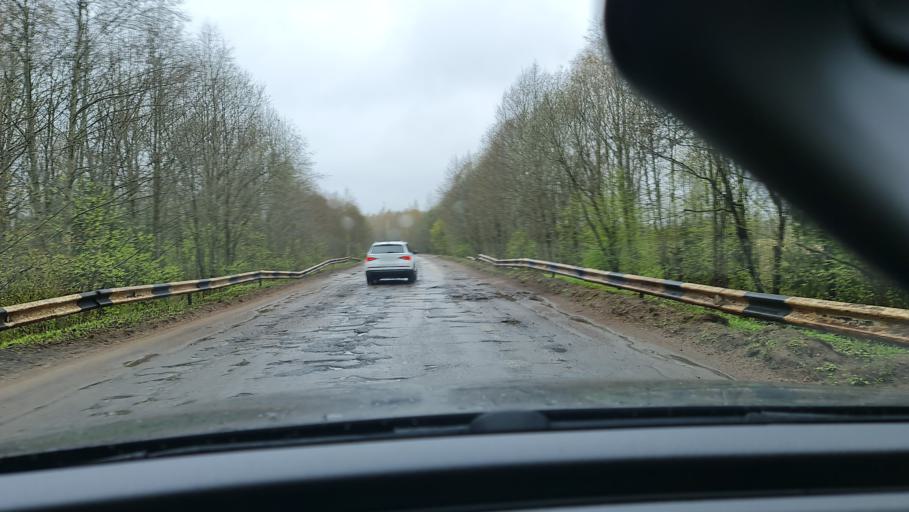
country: RU
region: Novgorod
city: Kresttsy
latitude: 57.9687
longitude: 32.7152
